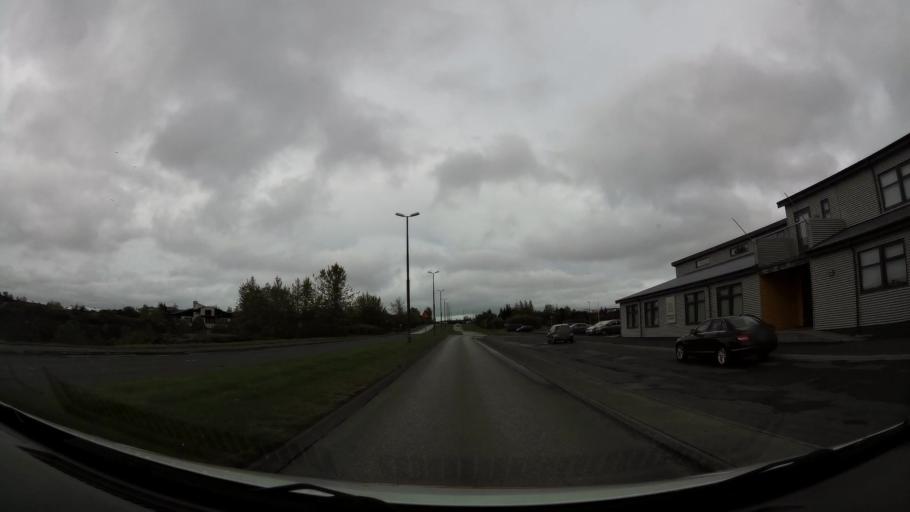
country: IS
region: Capital Region
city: Hafnarfjoerdur
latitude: 64.0749
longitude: -21.9663
